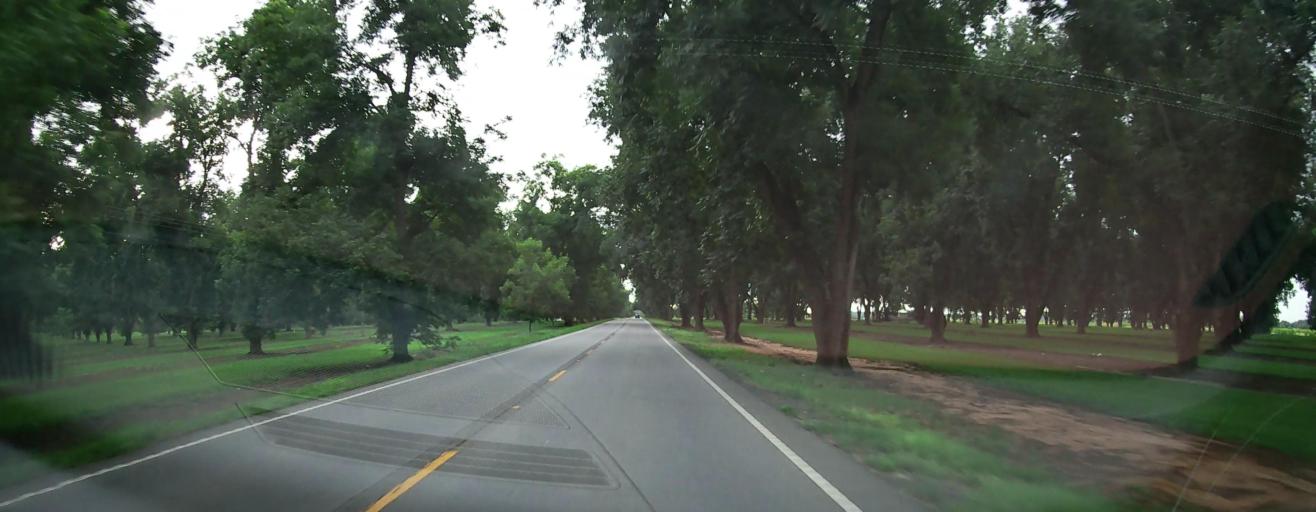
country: US
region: Georgia
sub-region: Houston County
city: Perry
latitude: 32.4407
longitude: -83.6575
